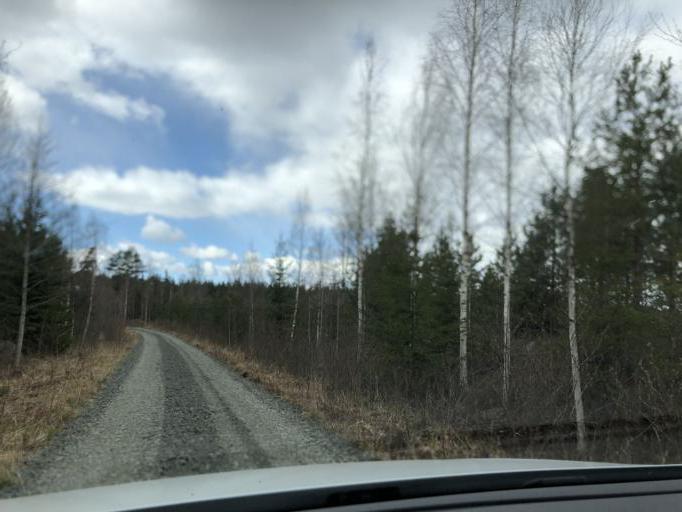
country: SE
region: Uppsala
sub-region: Heby Kommun
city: OEstervala
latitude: 60.3347
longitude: 17.1703
